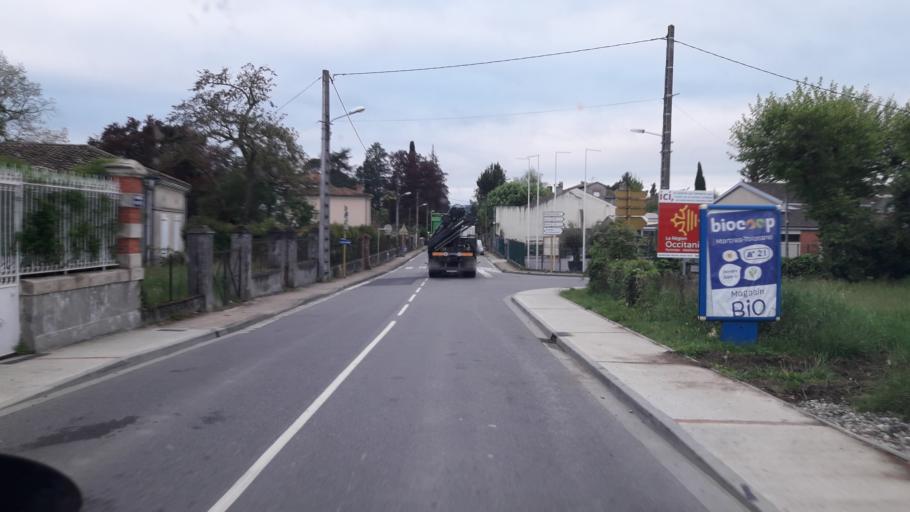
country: FR
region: Midi-Pyrenees
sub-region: Departement de la Haute-Garonne
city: Cazeres
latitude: 43.2135
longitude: 1.0854
